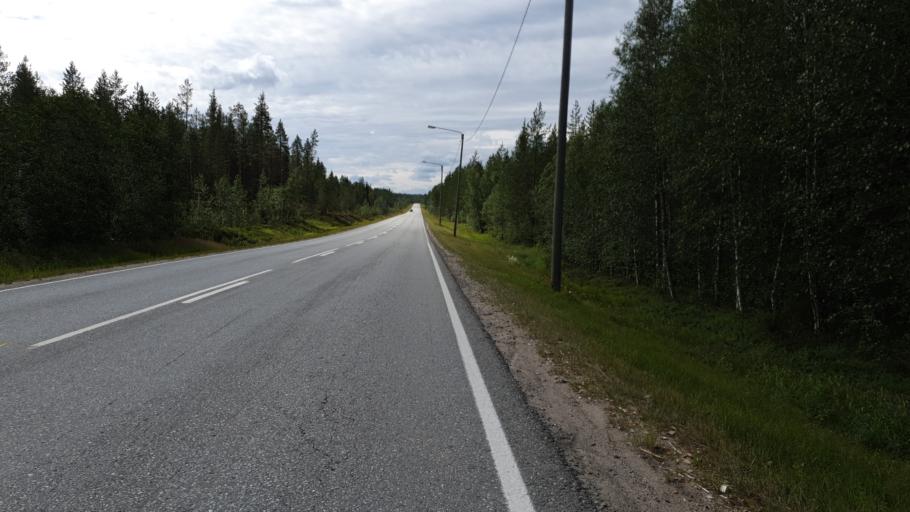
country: FI
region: Kainuu
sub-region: Kehys-Kainuu
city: Kuhmo
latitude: 64.5304
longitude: 29.9447
